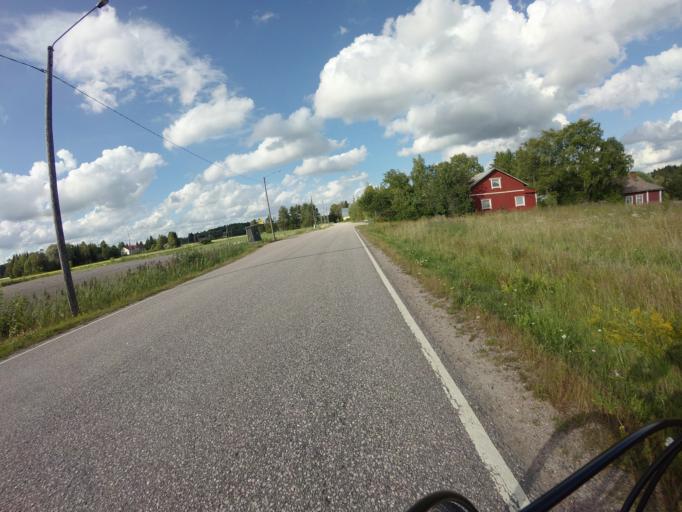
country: FI
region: Varsinais-Suomi
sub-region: Turku
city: Vahto
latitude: 60.5662
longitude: 22.3528
